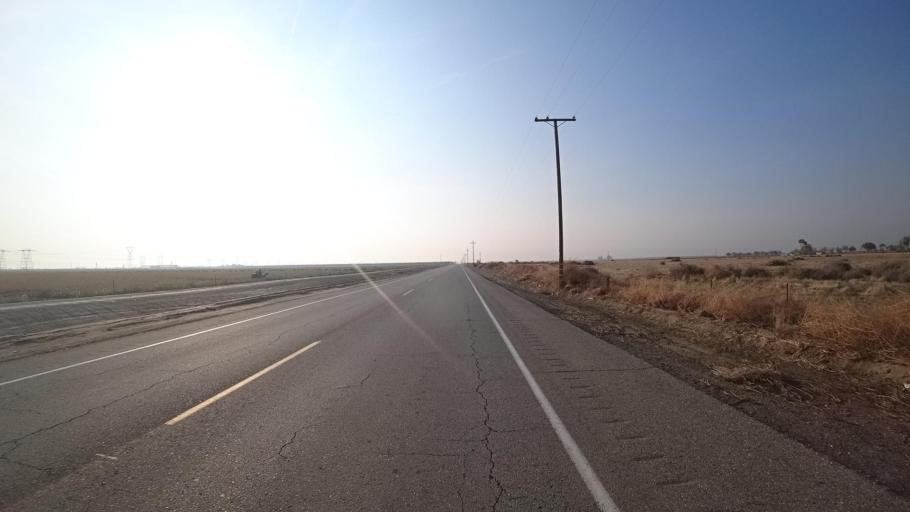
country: US
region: California
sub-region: Kern County
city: Weedpatch
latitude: 35.1689
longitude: -118.9148
